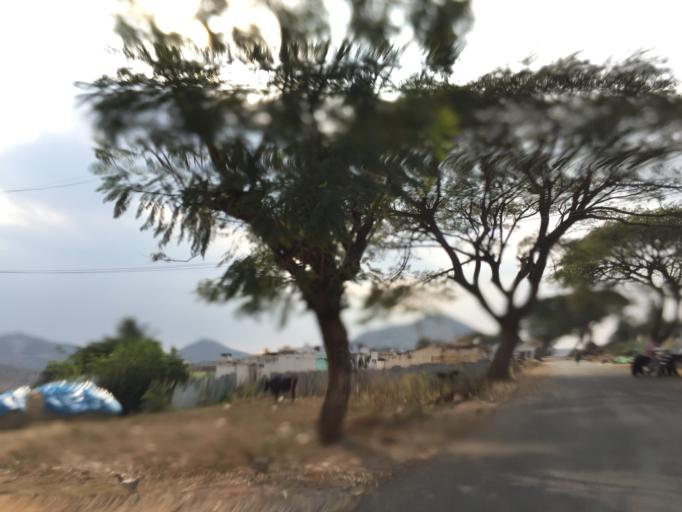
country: IN
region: Karnataka
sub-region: Chikkaballapur
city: Chik Ballapur
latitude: 13.5518
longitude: 77.7552
